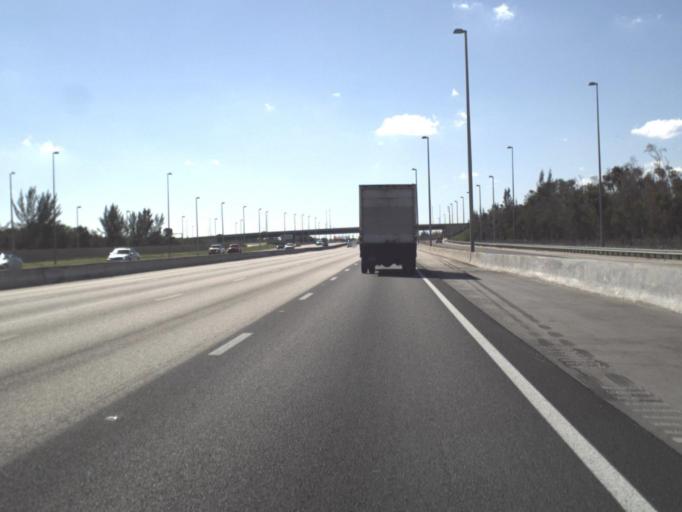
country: US
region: Florida
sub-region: Miami-Dade County
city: Doral
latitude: 25.8452
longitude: -80.3875
